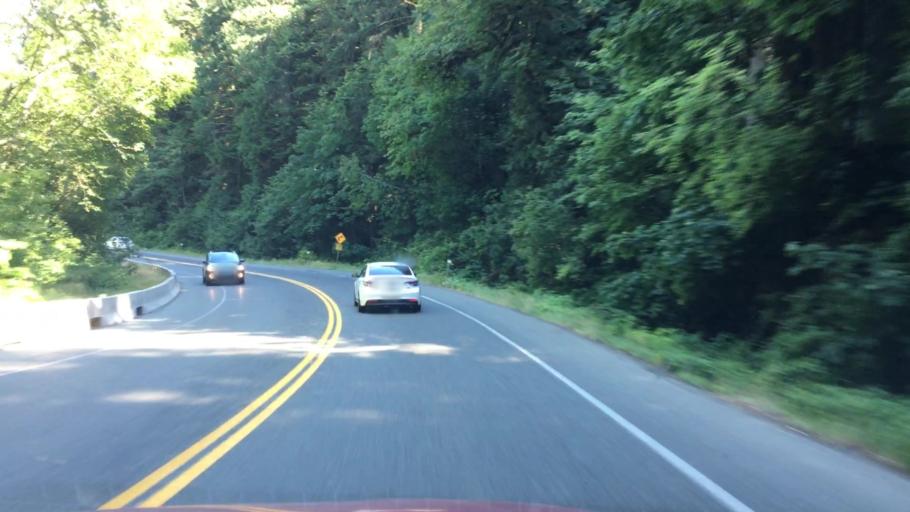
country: CA
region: British Columbia
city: Port Alberni
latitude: 49.2906
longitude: -124.6538
